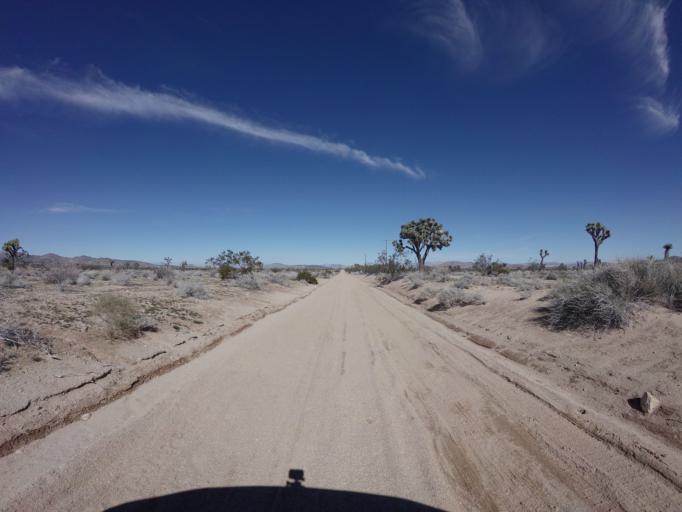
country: US
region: California
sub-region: San Bernardino County
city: Yucca Valley
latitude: 34.2243
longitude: -116.4046
